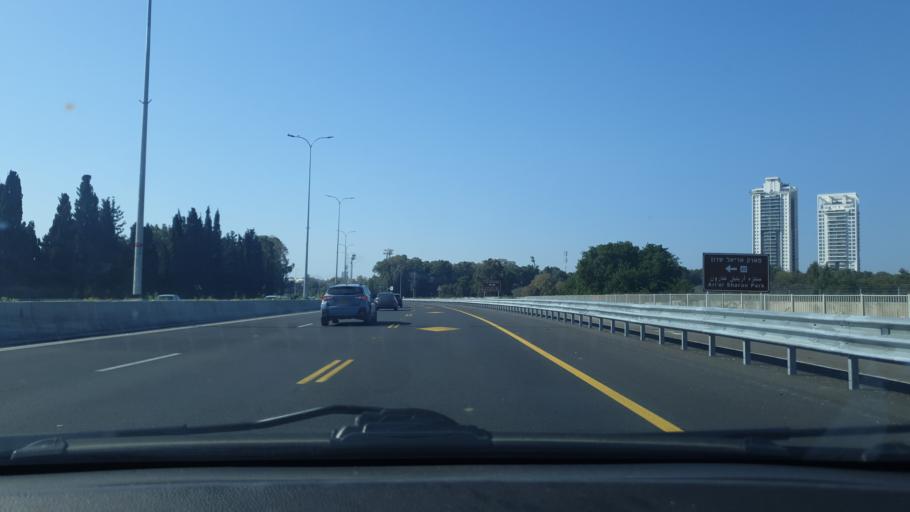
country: IL
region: Tel Aviv
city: Azor
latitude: 32.0420
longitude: 34.8207
